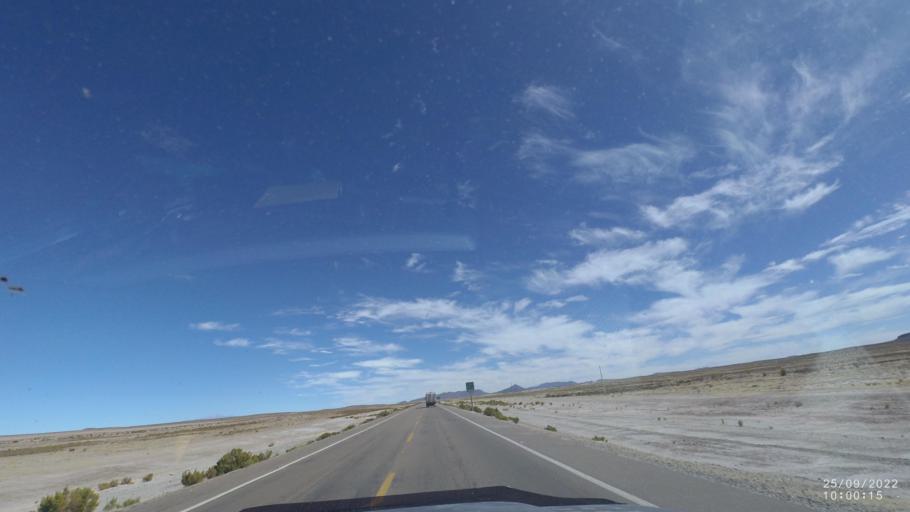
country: BO
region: Potosi
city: Colchani
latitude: -20.2769
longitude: -66.9455
